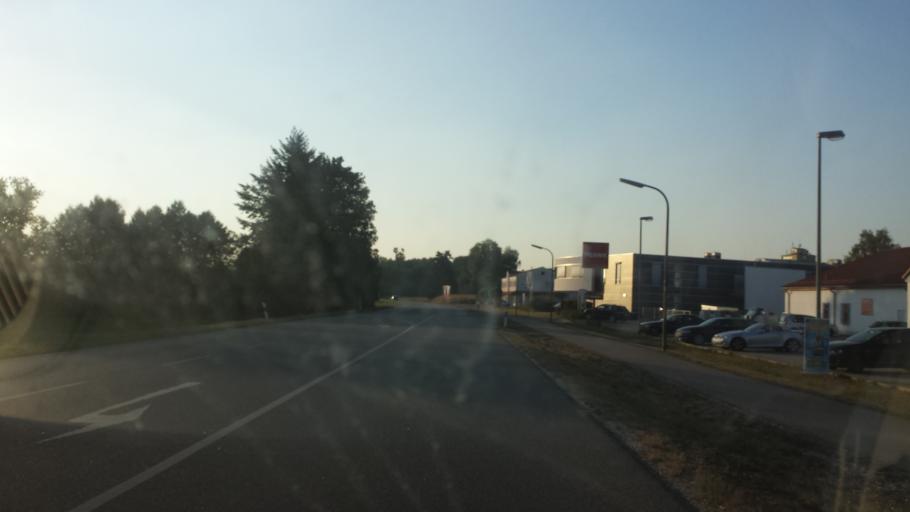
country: DE
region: Bavaria
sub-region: Upper Bavaria
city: Gaimersheim
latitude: 48.7951
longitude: 11.3729
